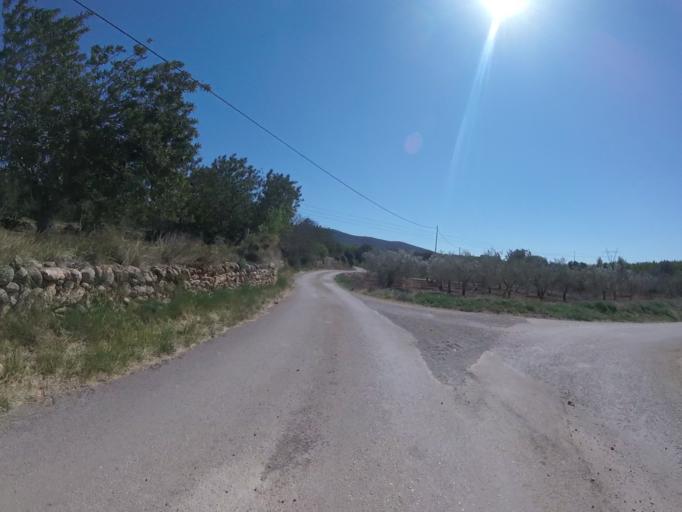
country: ES
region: Valencia
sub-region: Provincia de Castello
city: Cuevas de Vinroma
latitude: 40.3746
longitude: 0.1341
